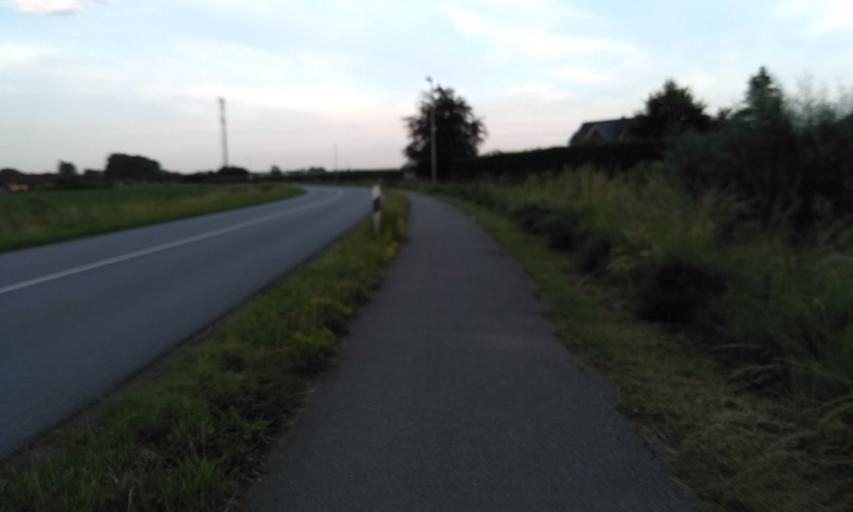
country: DE
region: Lower Saxony
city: Jork
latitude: 53.5119
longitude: 9.7200
